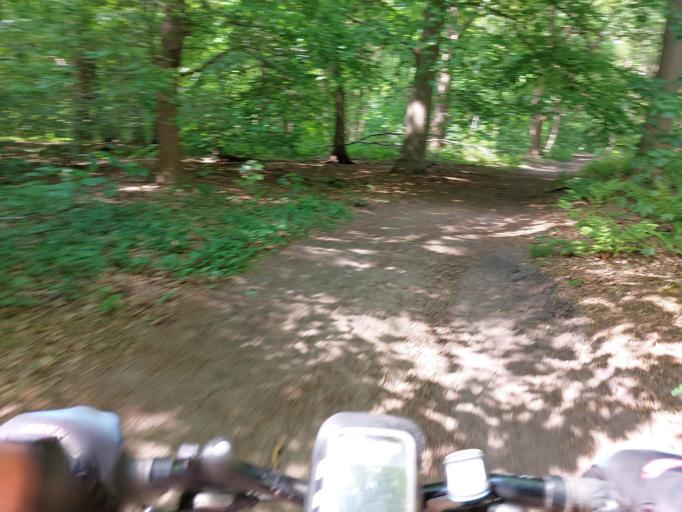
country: BE
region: Wallonia
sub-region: Province du Hainaut
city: Saint-Ghislain
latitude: 50.4832
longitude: 3.8154
